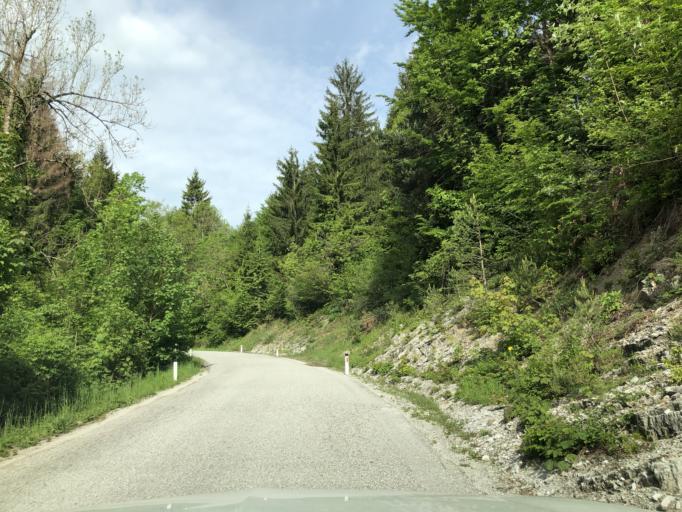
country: SI
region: Bloke
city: Nova Vas
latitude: 45.8003
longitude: 14.5557
